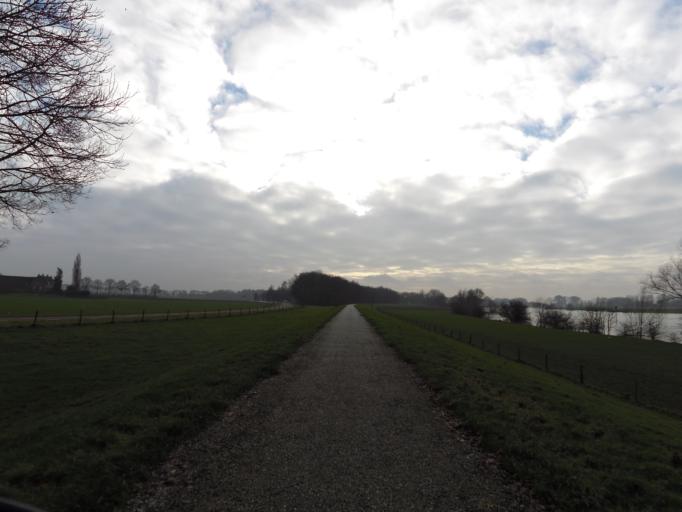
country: NL
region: Gelderland
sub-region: Gemeente Doesburg
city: Doesburg
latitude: 52.0000
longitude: 6.1147
